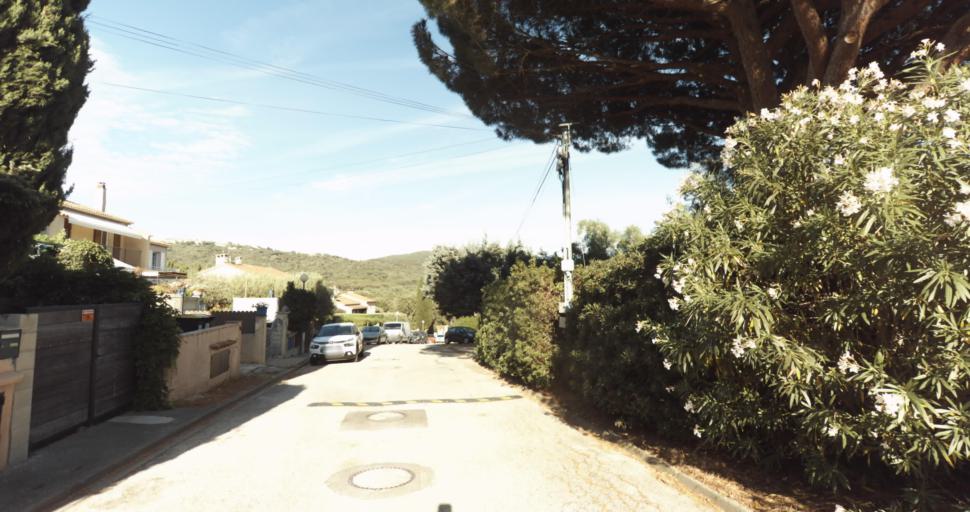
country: FR
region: Provence-Alpes-Cote d'Azur
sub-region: Departement du Var
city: La Croix-Valmer
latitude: 43.2242
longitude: 6.5673
